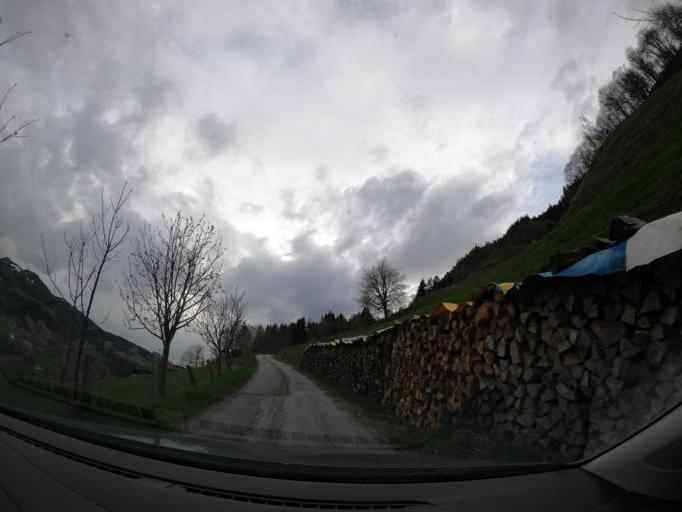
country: AT
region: Salzburg
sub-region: Politischer Bezirk Zell am See
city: Lend
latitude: 47.3019
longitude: 13.0644
